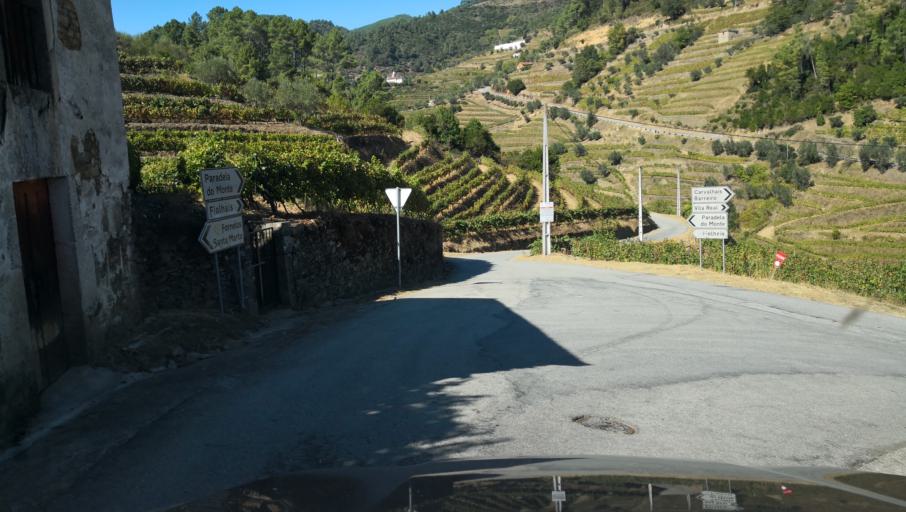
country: PT
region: Vila Real
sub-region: Santa Marta de Penaguiao
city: Santa Marta de Penaguiao
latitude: 41.2487
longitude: -7.8135
